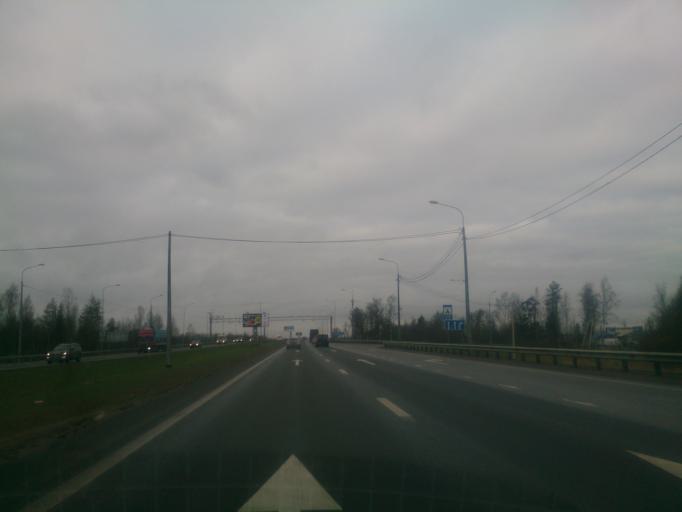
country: RU
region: Leningrad
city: Ul'yanovka
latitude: 59.6079
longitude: 30.7549
